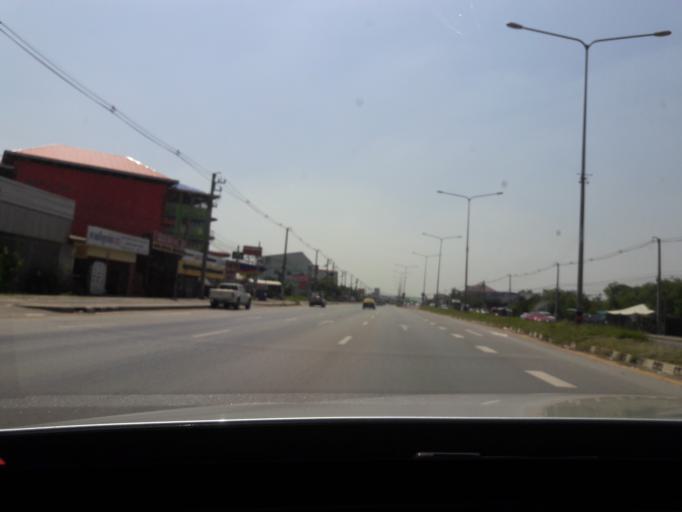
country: TH
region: Bangkok
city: Nong Khaem
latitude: 13.6647
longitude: 100.3147
